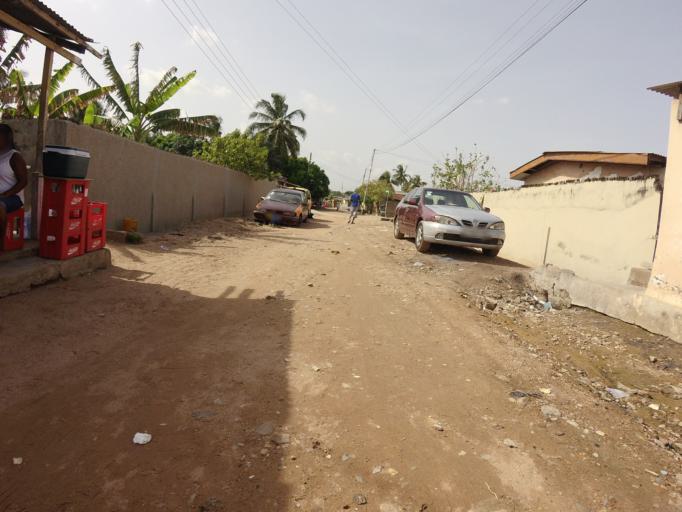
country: GH
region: Greater Accra
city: Dome
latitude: 5.6149
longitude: -0.2421
